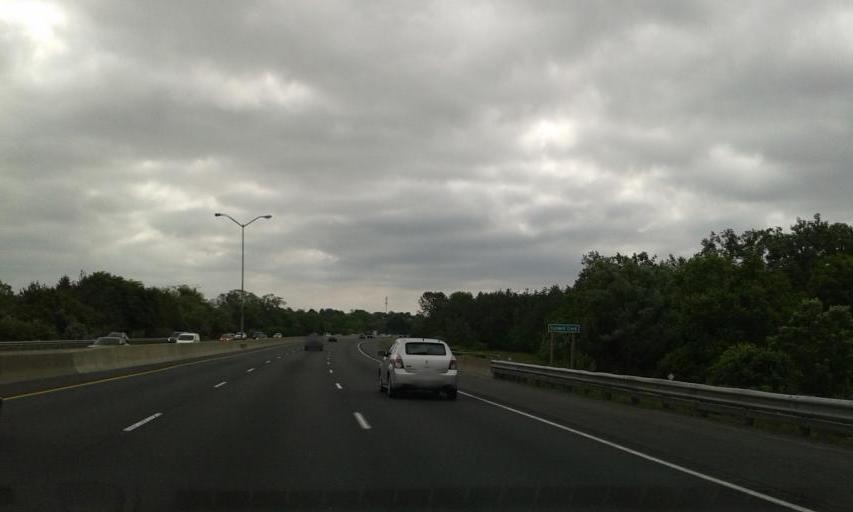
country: CA
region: Ontario
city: Oshawa
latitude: 43.8868
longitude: -78.8219
